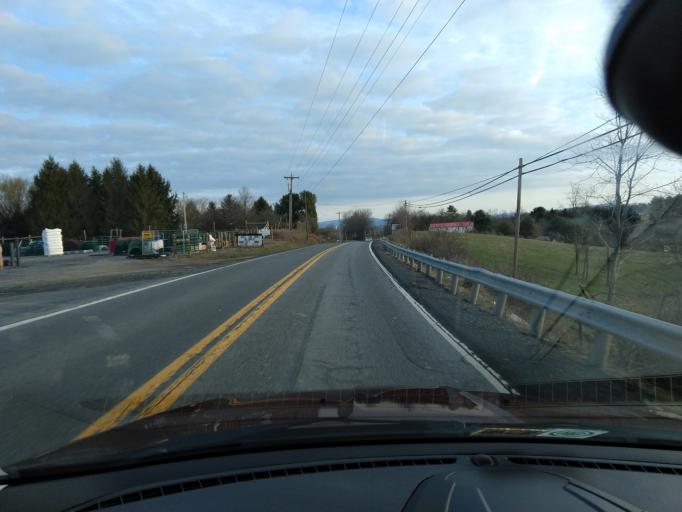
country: US
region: West Virginia
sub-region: Greenbrier County
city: Lewisburg
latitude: 37.9150
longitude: -80.3843
